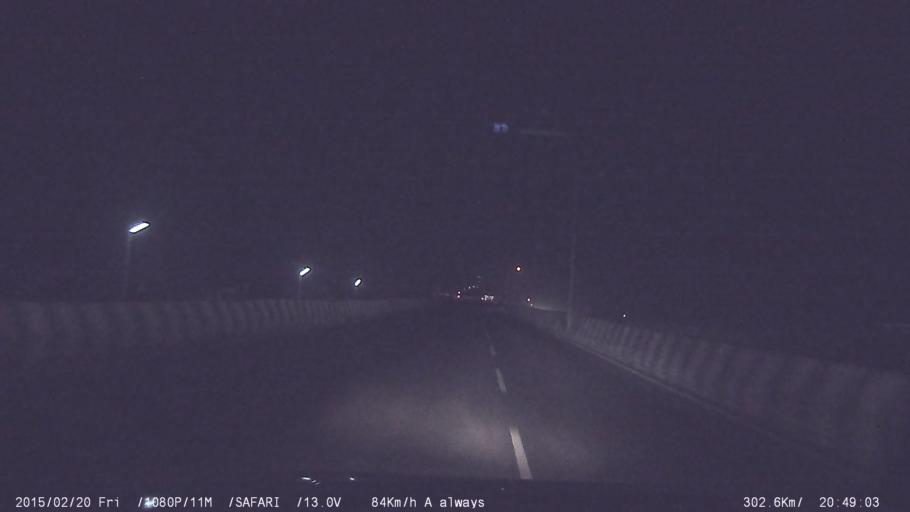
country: IN
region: Tamil Nadu
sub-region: Erode
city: Bhavani
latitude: 11.4254
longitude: 77.6759
